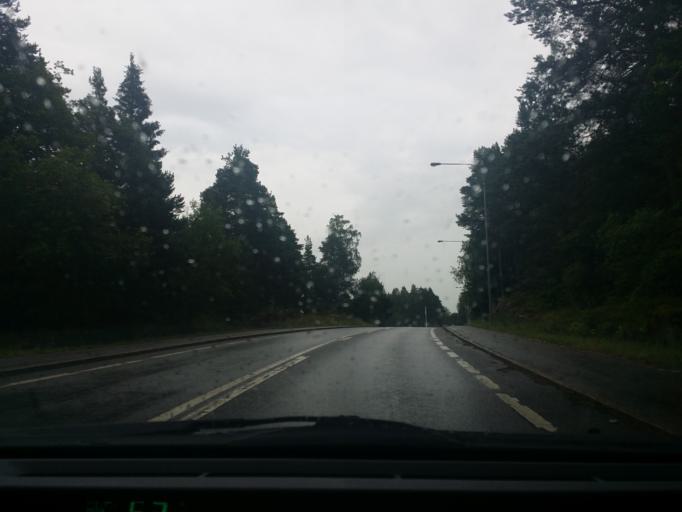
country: SE
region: OErebro
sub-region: Lindesbergs Kommun
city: Frovi
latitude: 59.4688
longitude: 15.3500
